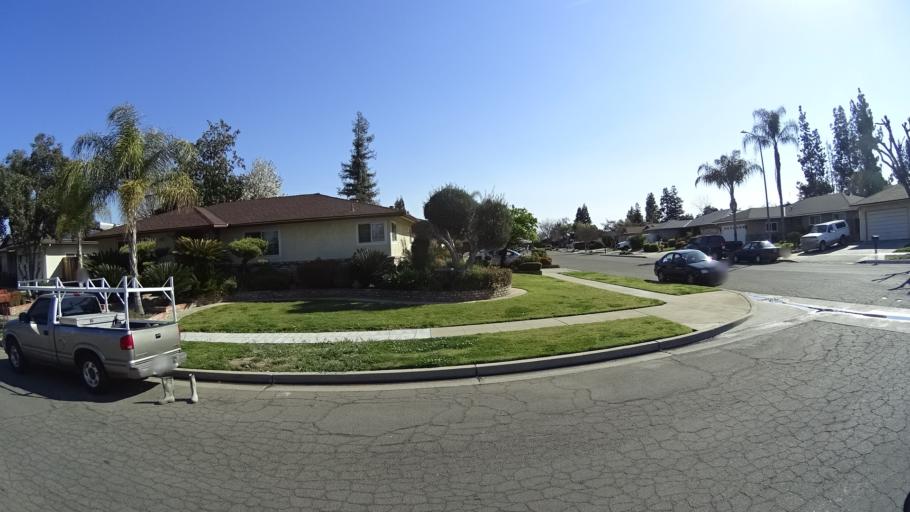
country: US
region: California
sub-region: Fresno County
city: Clovis
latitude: 36.8341
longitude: -119.7500
